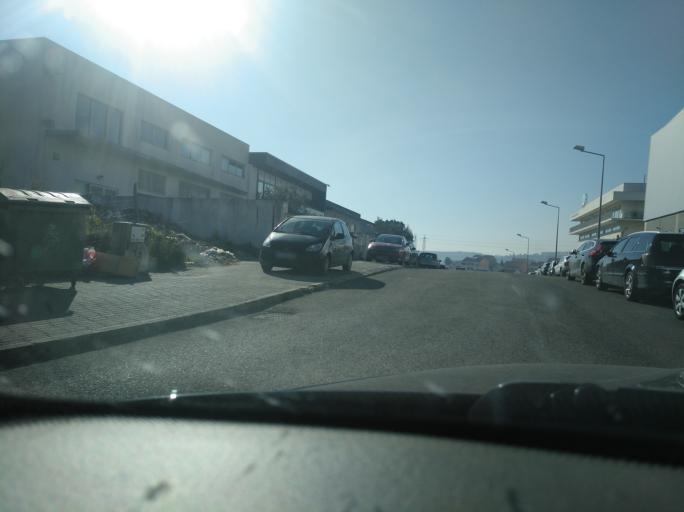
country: PT
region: Lisbon
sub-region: Odivelas
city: Famoes
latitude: 38.7918
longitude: -9.2173
